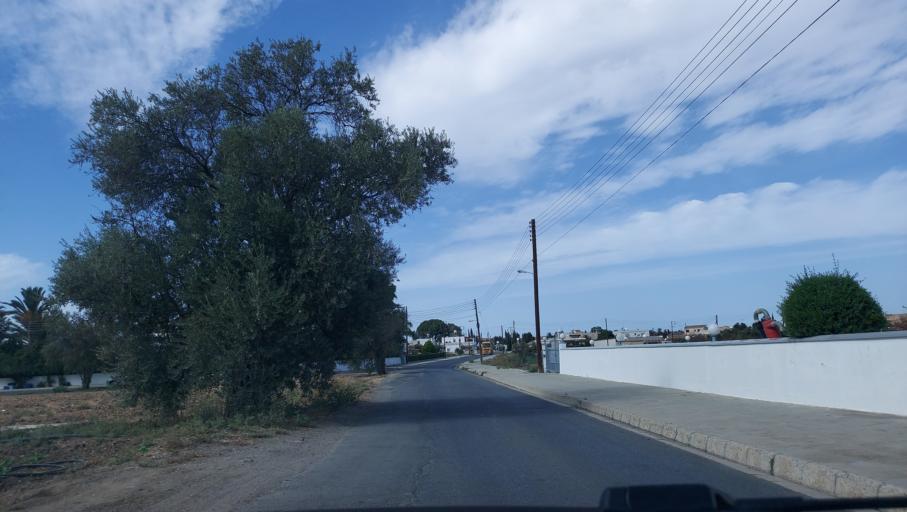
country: CY
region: Lefkosia
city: Pano Deftera
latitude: 35.0776
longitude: 33.2675
